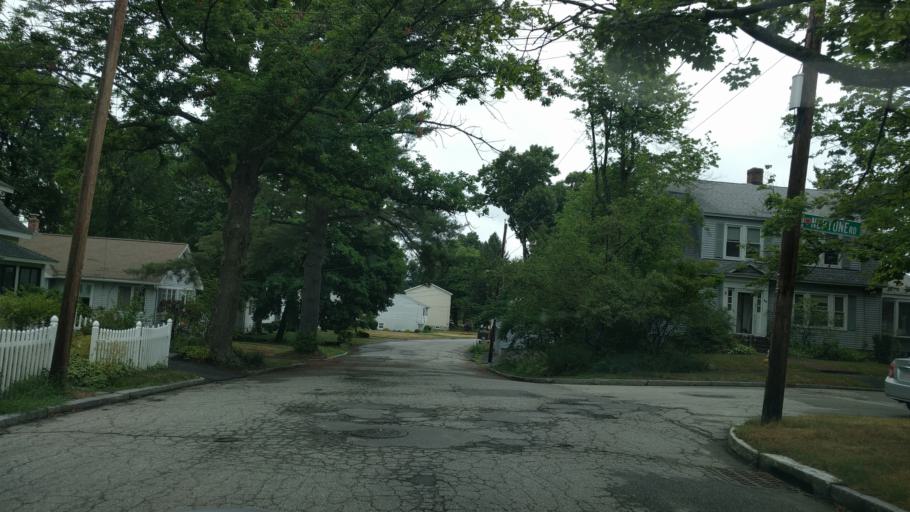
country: US
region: Massachusetts
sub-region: Worcester County
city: Worcester
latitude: 42.2922
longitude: -71.8207
